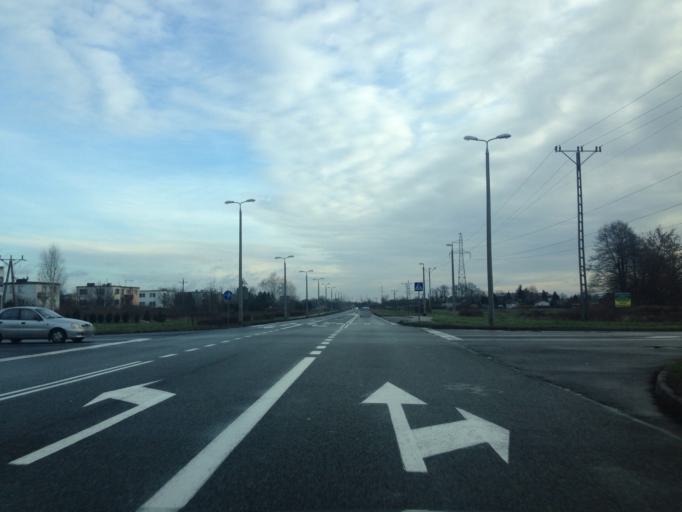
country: PL
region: Kujawsko-Pomorskie
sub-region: Torun
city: Torun
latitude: 52.9906
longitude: 18.6158
